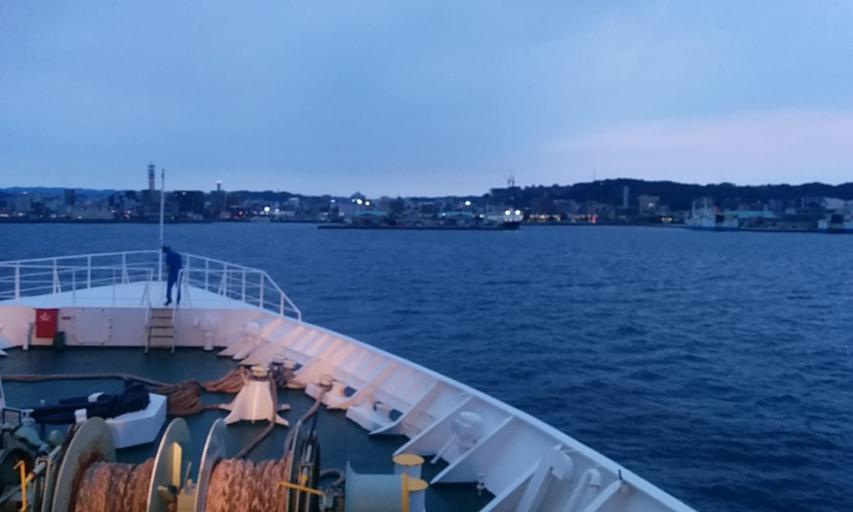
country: JP
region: Kagoshima
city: Kagoshima-shi
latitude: 31.5920
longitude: 130.5738
